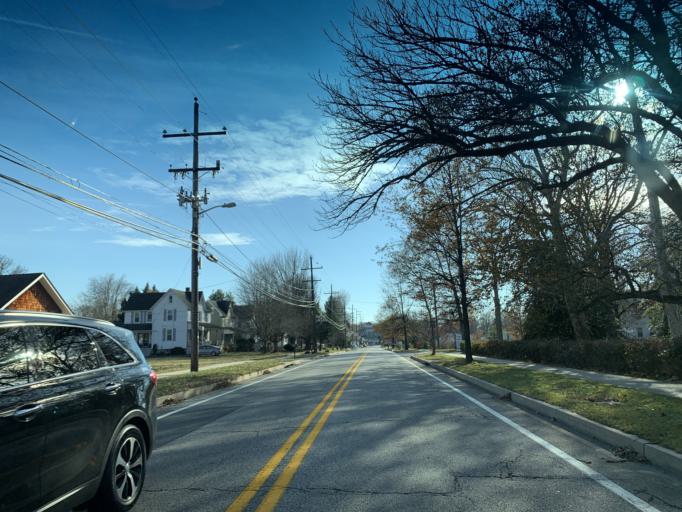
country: US
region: Maryland
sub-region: Cecil County
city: Perryville
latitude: 39.5640
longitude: -76.0710
